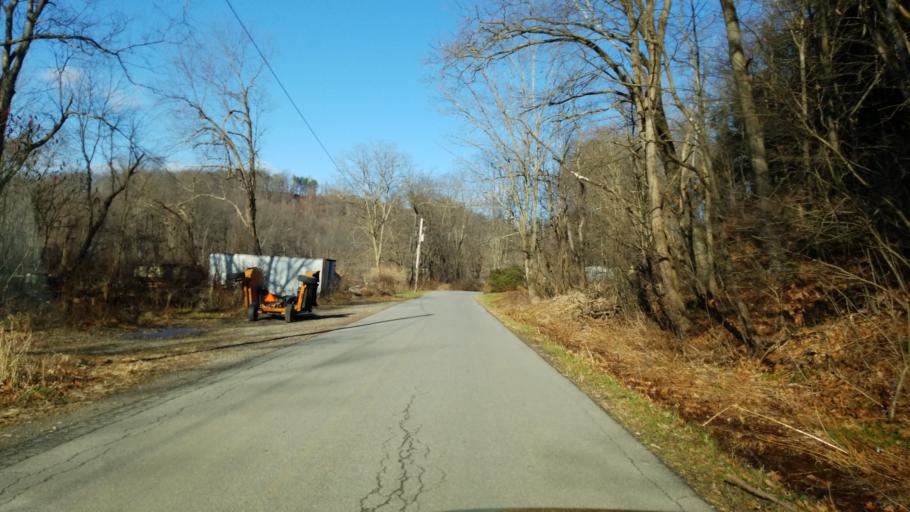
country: US
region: Pennsylvania
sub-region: Clearfield County
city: Curwensville
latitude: 40.9776
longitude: -78.4926
